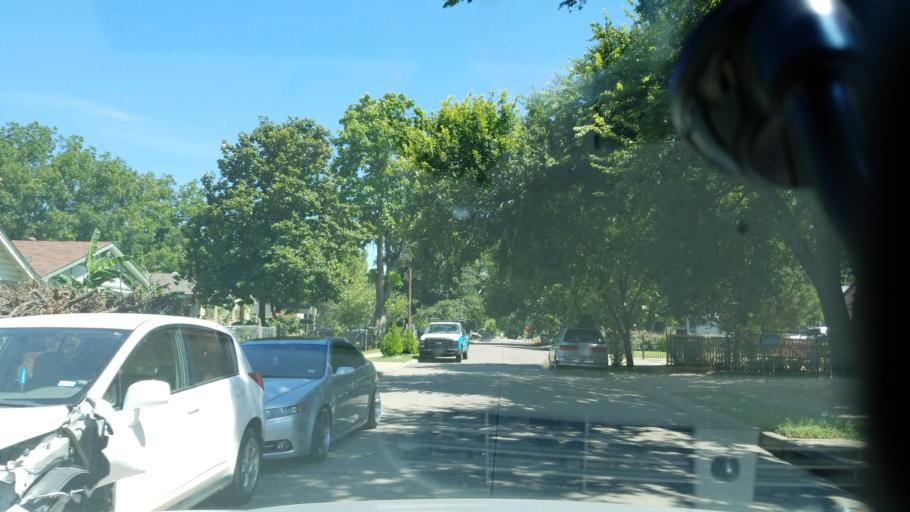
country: US
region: Texas
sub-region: Dallas County
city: Dallas
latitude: 32.7082
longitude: -96.8159
